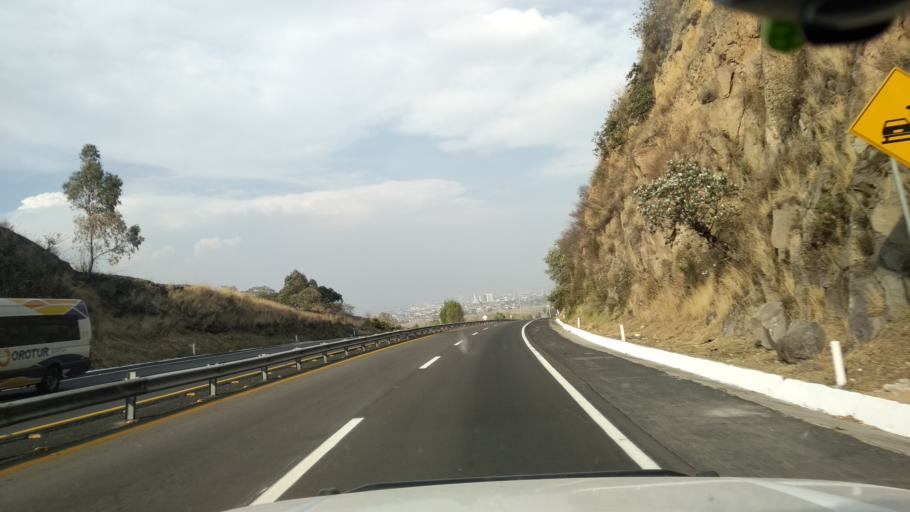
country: MX
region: Puebla
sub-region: Ocoyucan
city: Santa Martha Hidalgo
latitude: 18.9811
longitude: -98.3219
